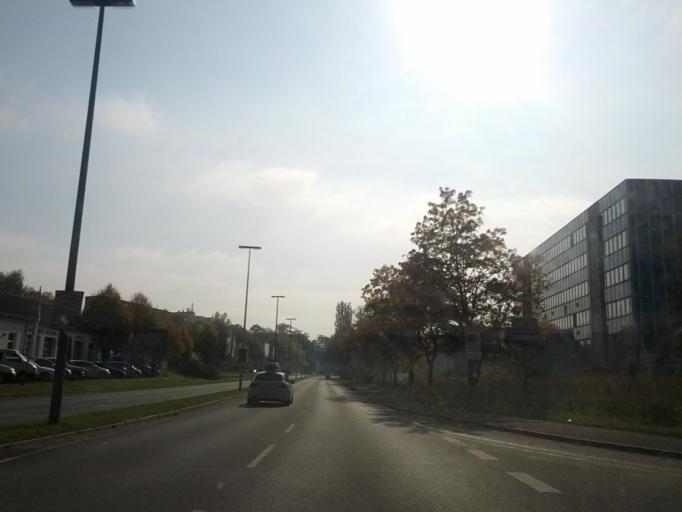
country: DE
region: Thuringia
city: Gera
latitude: 50.9027
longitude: 12.0693
